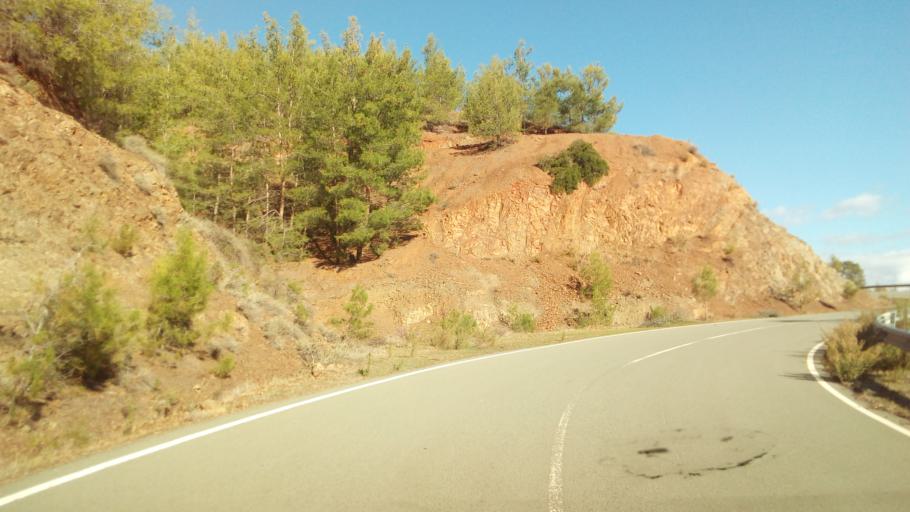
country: CY
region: Lefkosia
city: Lefka
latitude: 35.0969
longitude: 32.7572
